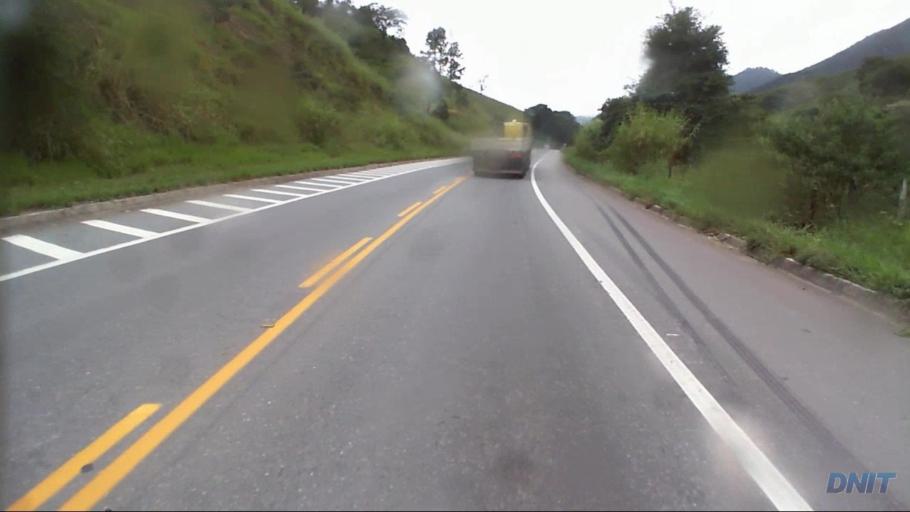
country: BR
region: Minas Gerais
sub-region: Nova Era
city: Nova Era
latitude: -19.7160
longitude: -43.0016
